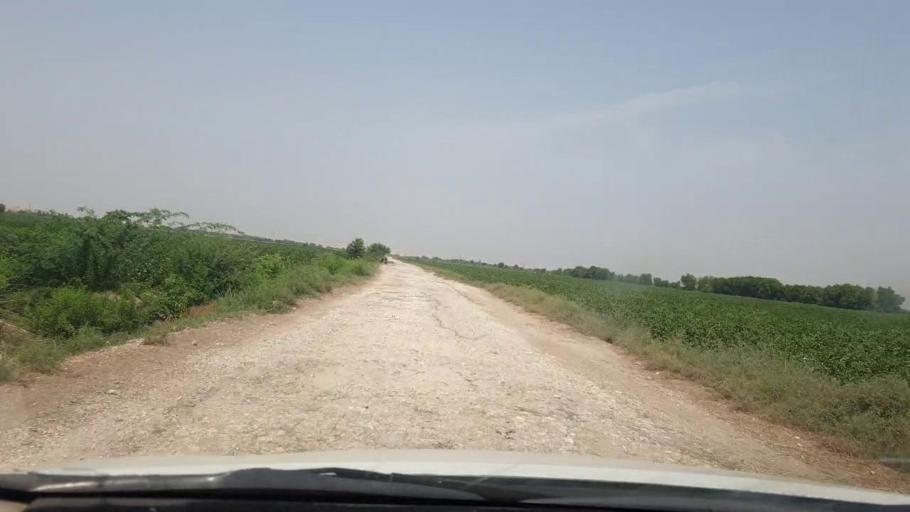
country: PK
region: Sindh
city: Rohri
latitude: 27.4977
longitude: 69.0179
